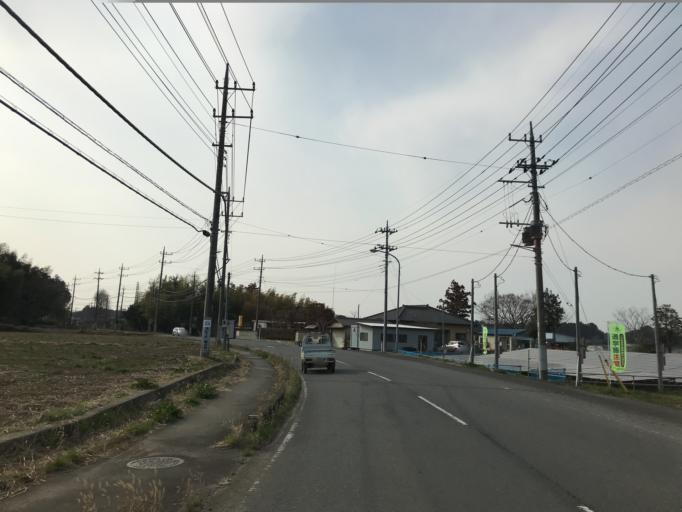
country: JP
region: Ibaraki
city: Okunoya
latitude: 36.2346
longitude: 140.3738
